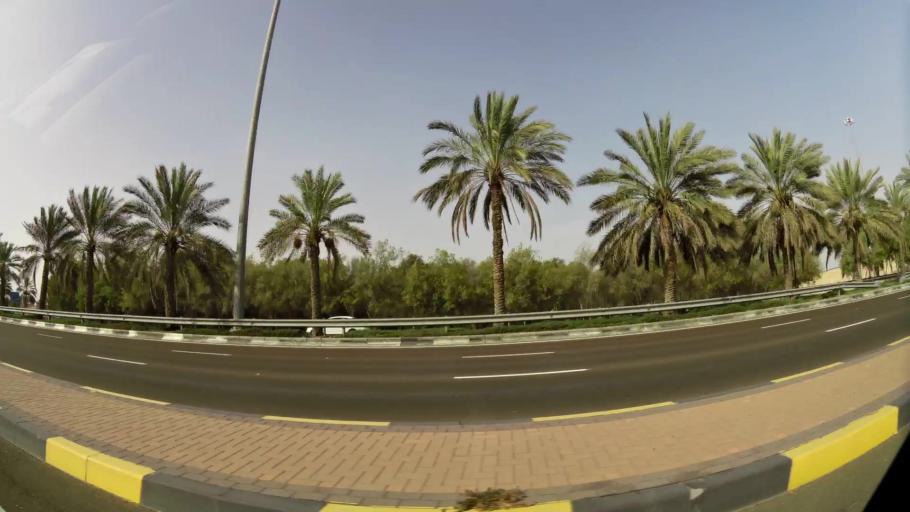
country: AE
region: Abu Dhabi
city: Al Ain
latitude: 24.1848
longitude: 55.5957
